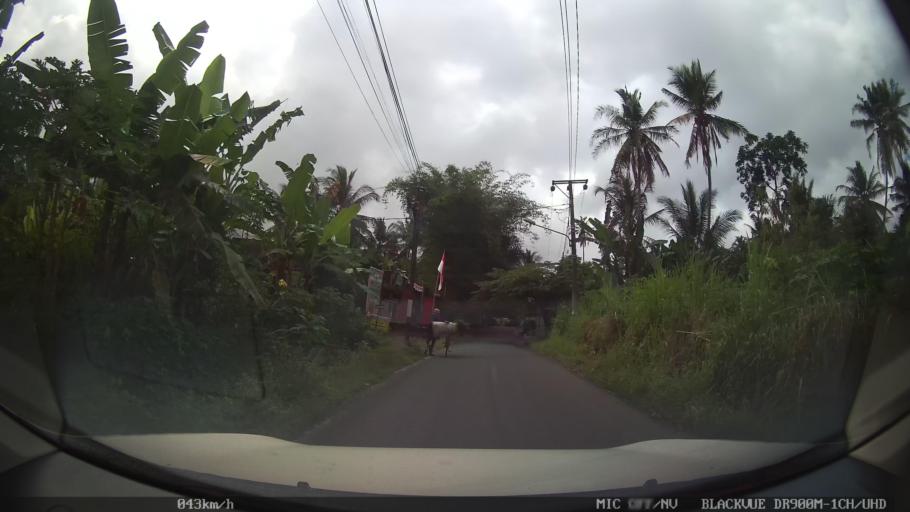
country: ID
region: Bali
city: Banjar Parekan
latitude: -8.5690
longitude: 115.2049
